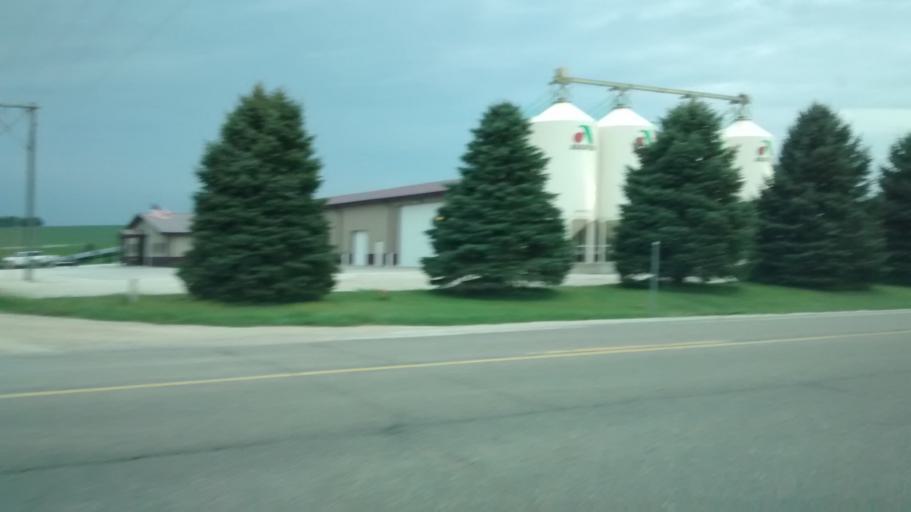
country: US
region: Iowa
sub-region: Plymouth County
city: Kingsley
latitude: 42.5831
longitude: -95.9780
